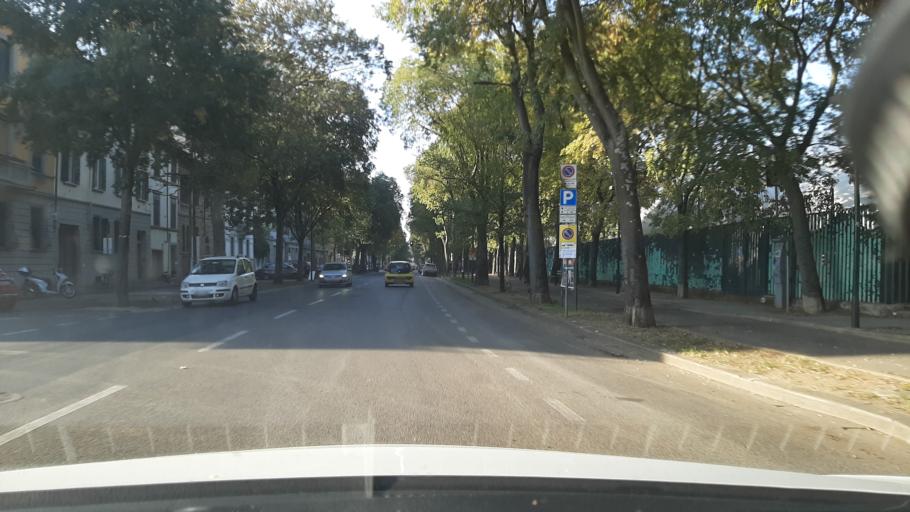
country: IT
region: Tuscany
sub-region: Province of Florence
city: Fiesole
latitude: 43.7785
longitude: 11.2878
